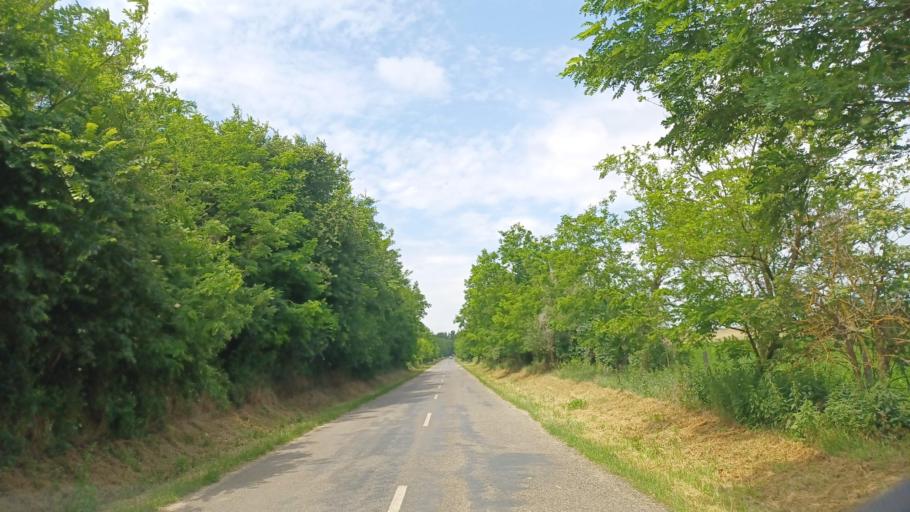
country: HU
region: Tolna
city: Simontornya
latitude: 46.7042
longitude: 18.5126
